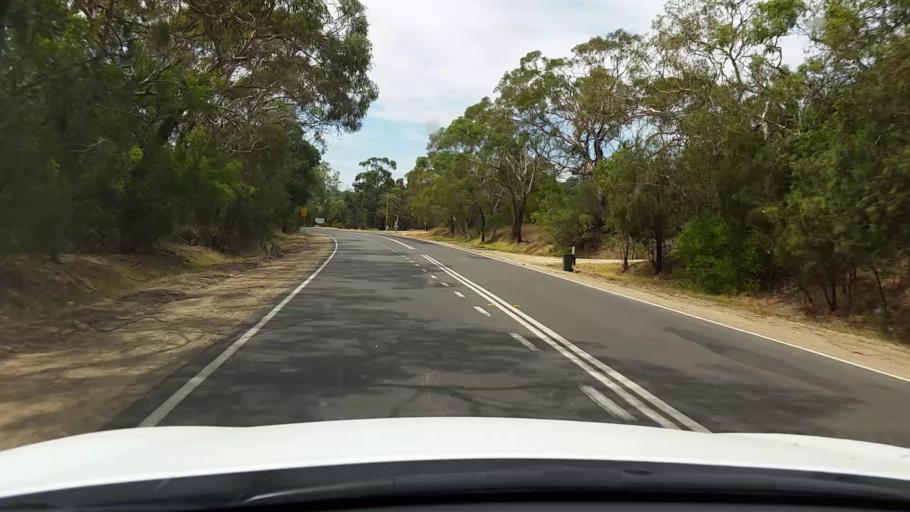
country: AU
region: Victoria
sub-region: Mornington Peninsula
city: Mount Martha
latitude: -38.2840
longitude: 145.0666
